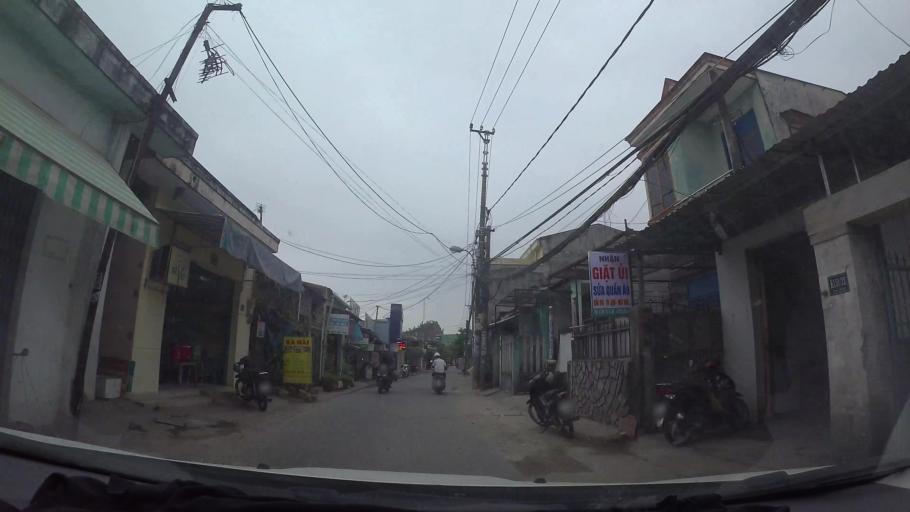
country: VN
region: Da Nang
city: Lien Chieu
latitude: 16.0695
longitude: 108.1431
